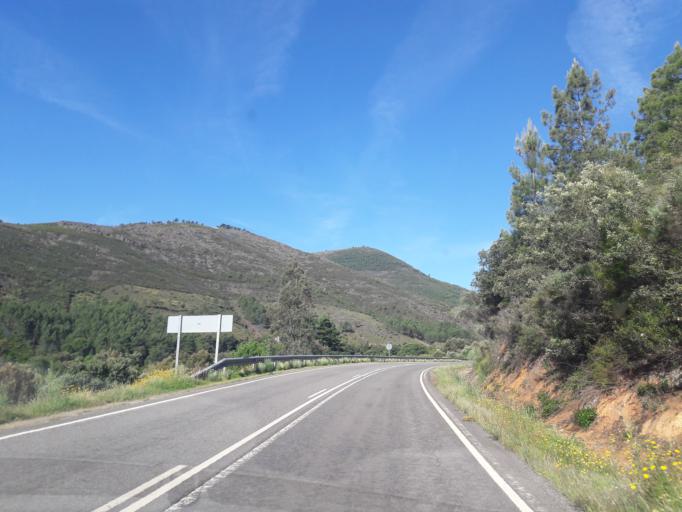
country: ES
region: Castille and Leon
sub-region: Provincia de Salamanca
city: Herguijuela de la Sierra
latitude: 40.4036
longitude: -6.0790
